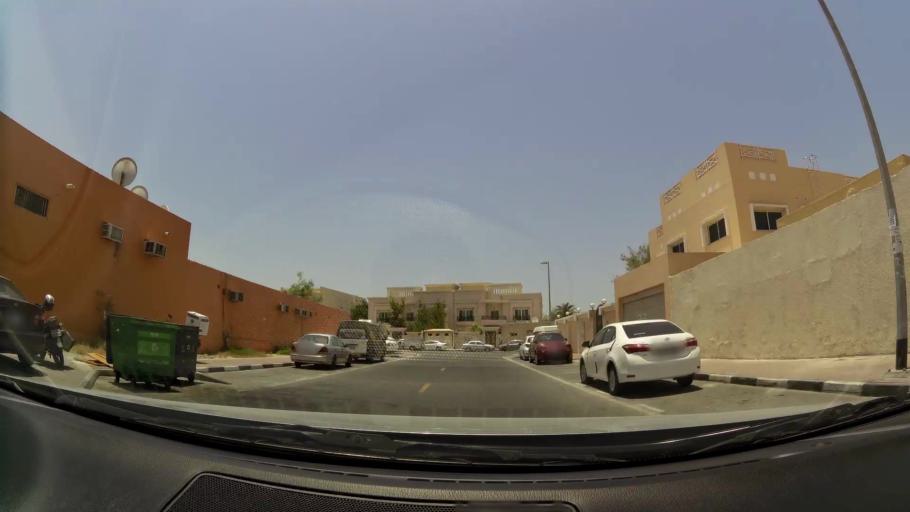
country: AE
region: Ash Shariqah
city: Sharjah
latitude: 25.2278
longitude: 55.2650
